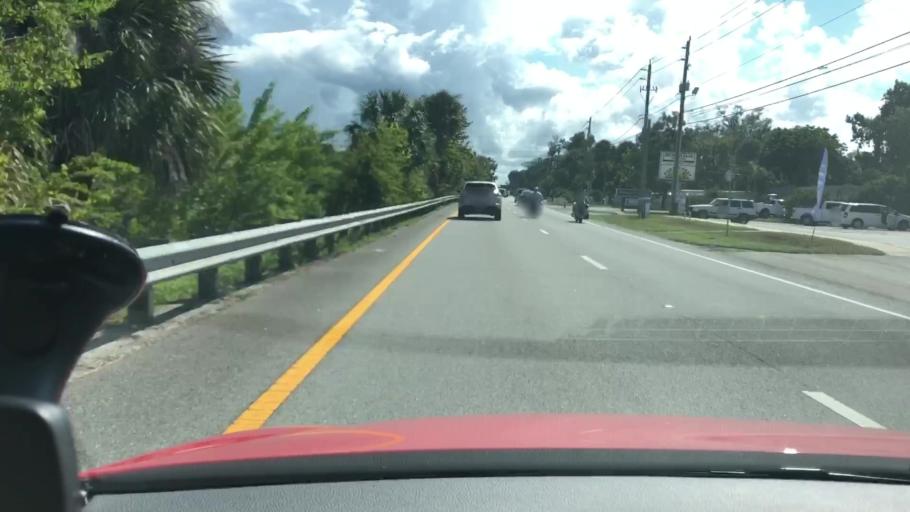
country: US
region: Florida
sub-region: Volusia County
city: South Daytona
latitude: 29.1528
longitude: -81.0189
